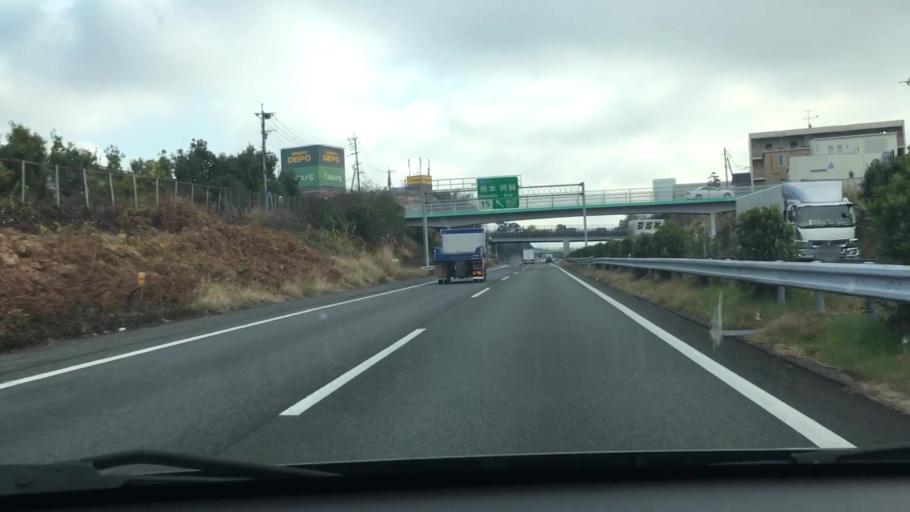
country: JP
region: Kumamoto
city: Kumamoto
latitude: 32.8383
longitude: 130.7767
